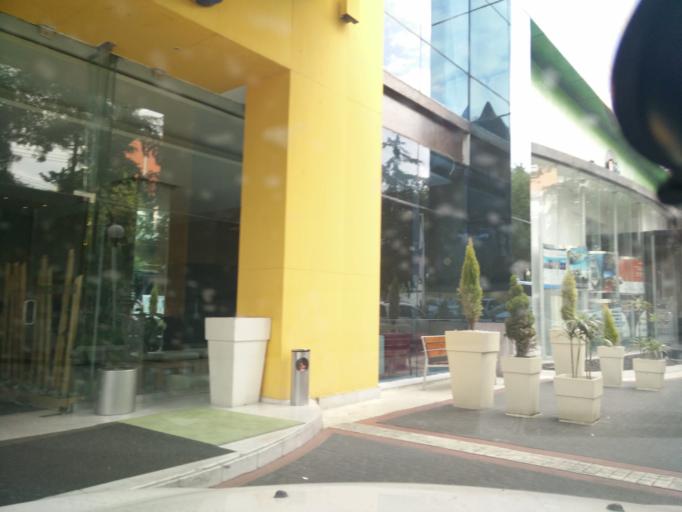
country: MX
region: Mexico City
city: Colonia del Valle
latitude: 19.3956
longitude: -99.1746
